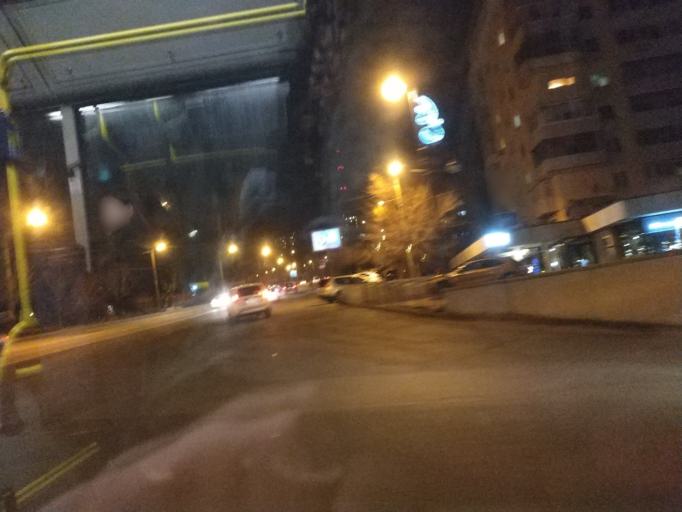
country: RU
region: Primorskiy
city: Vladivostok
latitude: 43.1241
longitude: 131.8886
